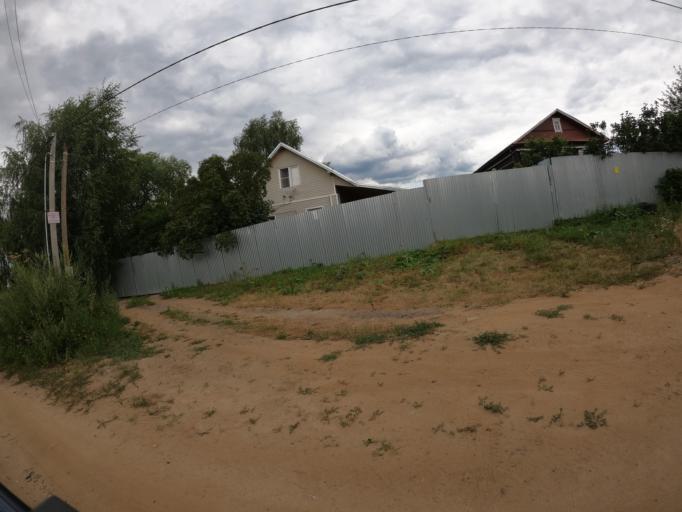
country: RU
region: Moskovskaya
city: Bronnitsy
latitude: 55.4868
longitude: 38.2569
